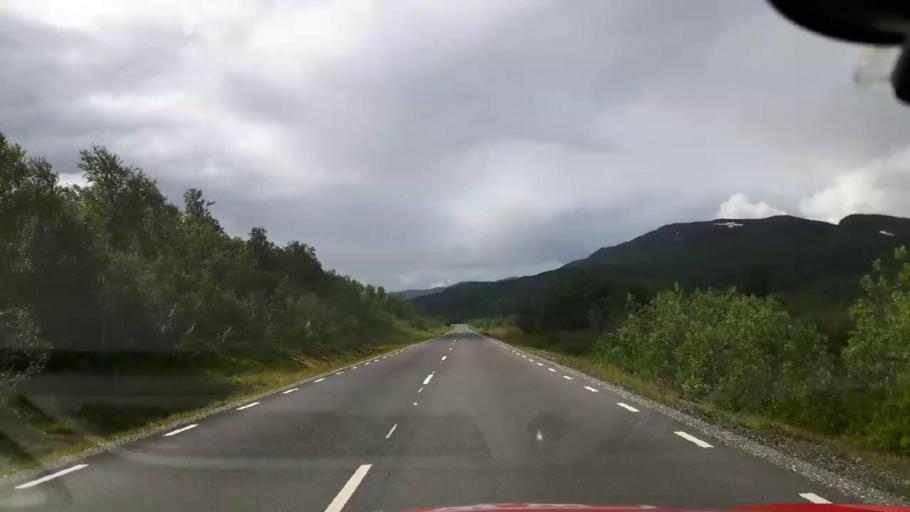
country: NO
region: Nordland
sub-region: Hattfjelldal
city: Hattfjelldal
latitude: 64.9925
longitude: 14.2270
